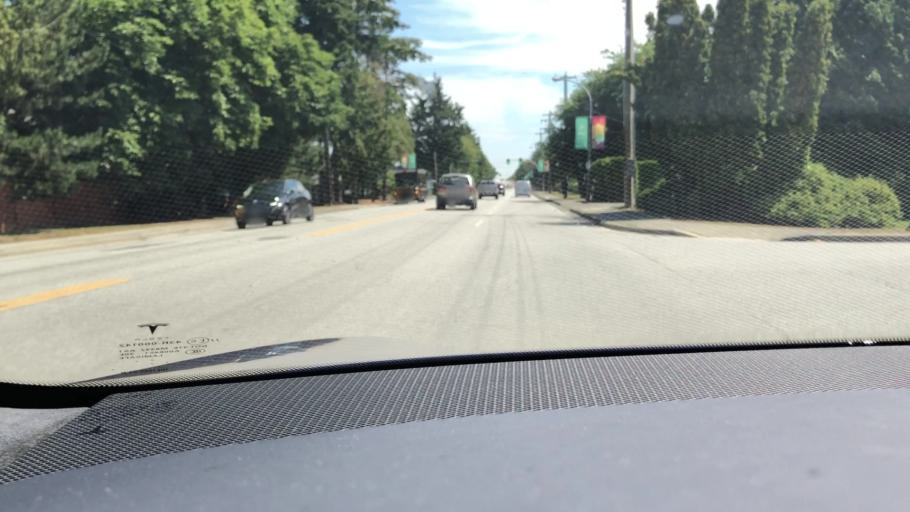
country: CA
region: British Columbia
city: Richmond
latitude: 49.1845
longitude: -123.0886
